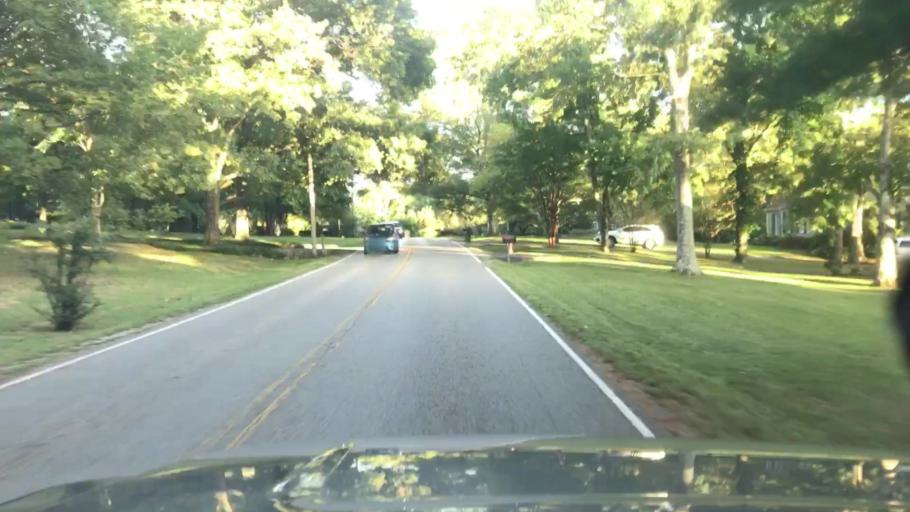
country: US
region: Tennessee
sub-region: Davidson County
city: Belle Meade
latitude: 36.1259
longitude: -86.8581
